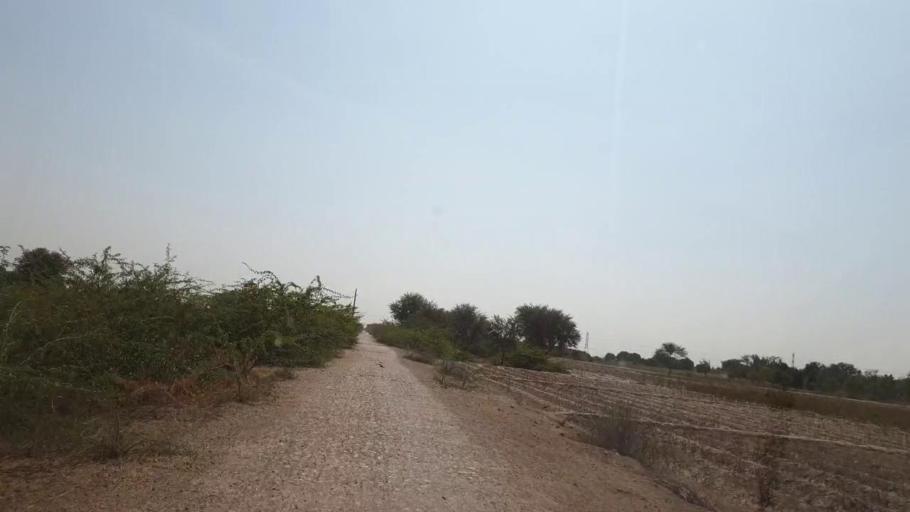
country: PK
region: Sindh
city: Nabisar
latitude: 25.0655
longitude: 69.5526
